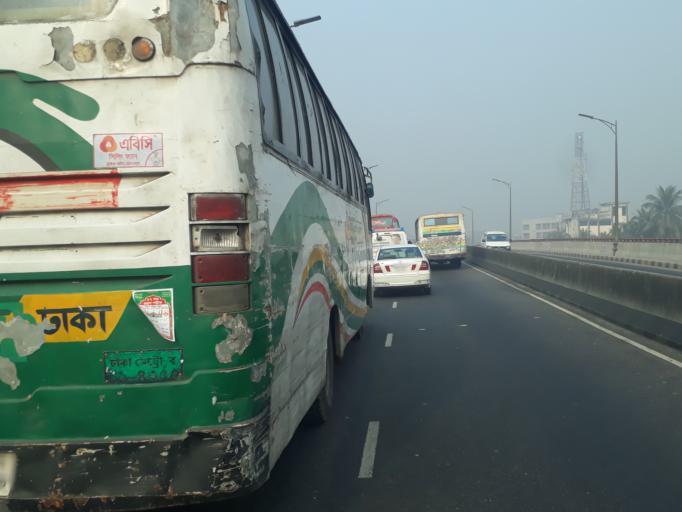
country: BD
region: Dhaka
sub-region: Dhaka
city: Dhaka
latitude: 23.7086
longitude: 90.4376
